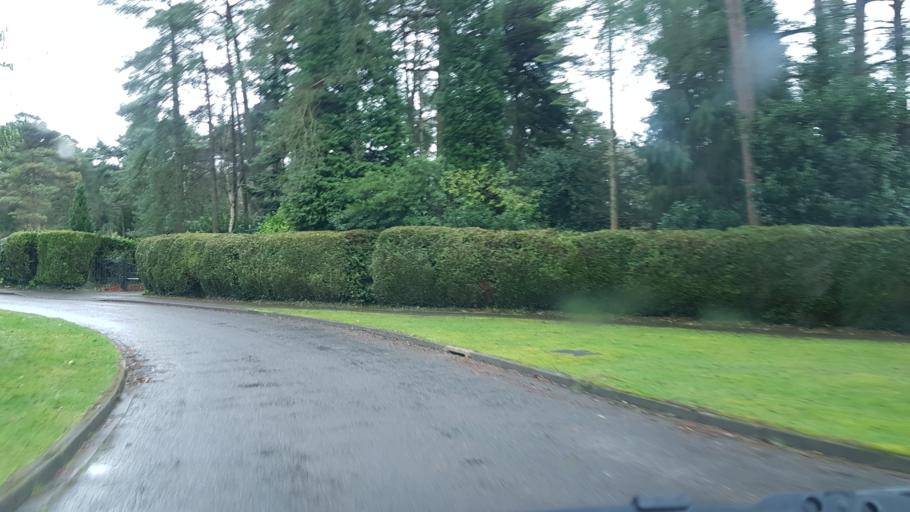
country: GB
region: England
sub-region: Surrey
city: Hindhead
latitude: 51.1062
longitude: -0.7571
